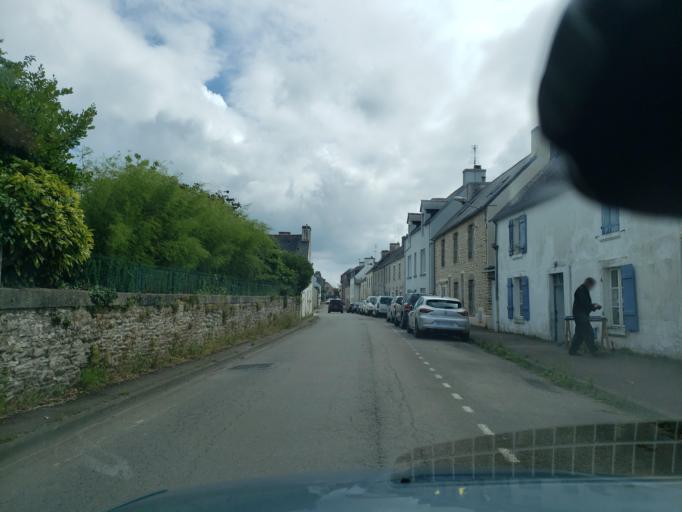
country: FR
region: Brittany
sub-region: Departement du Finistere
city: Ploneour-Lanvern
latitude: 47.9056
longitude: -4.2822
